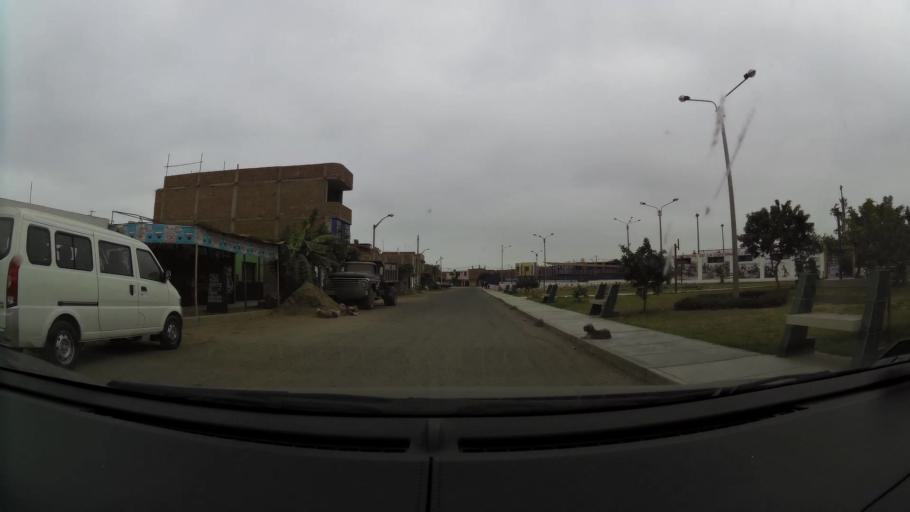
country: PE
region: La Libertad
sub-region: Provincia de Trujillo
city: La Esperanza
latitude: -8.0794
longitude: -79.0577
